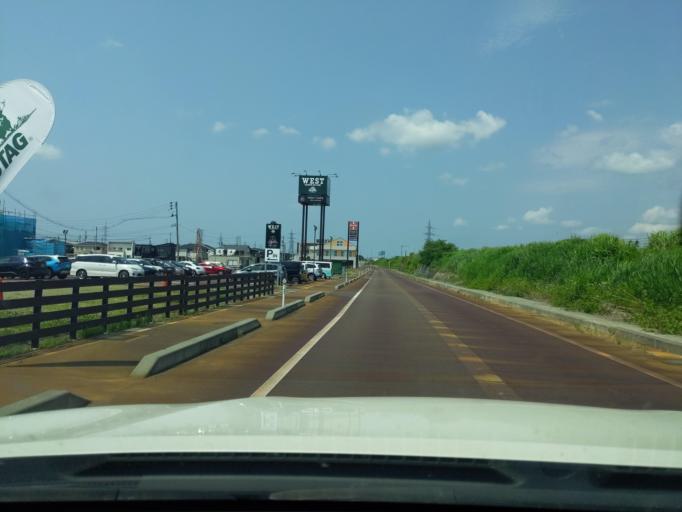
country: JP
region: Niigata
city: Nagaoka
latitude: 37.4274
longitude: 138.8643
